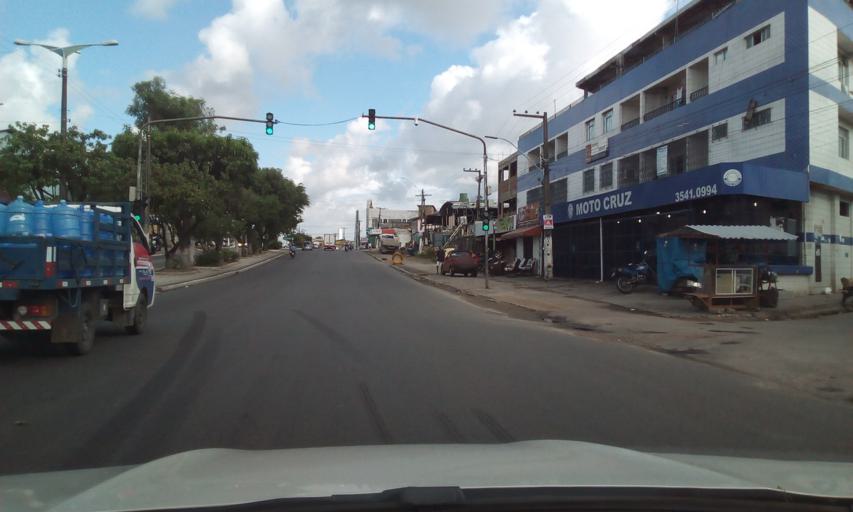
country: BR
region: Pernambuco
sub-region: Abreu E Lima
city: Abreu e Lima
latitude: -7.9073
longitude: -34.9022
